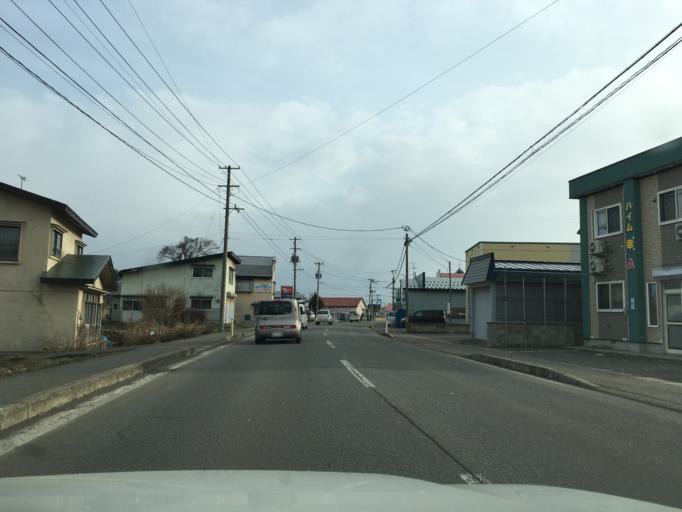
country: JP
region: Aomori
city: Namioka
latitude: 40.7155
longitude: 140.5909
